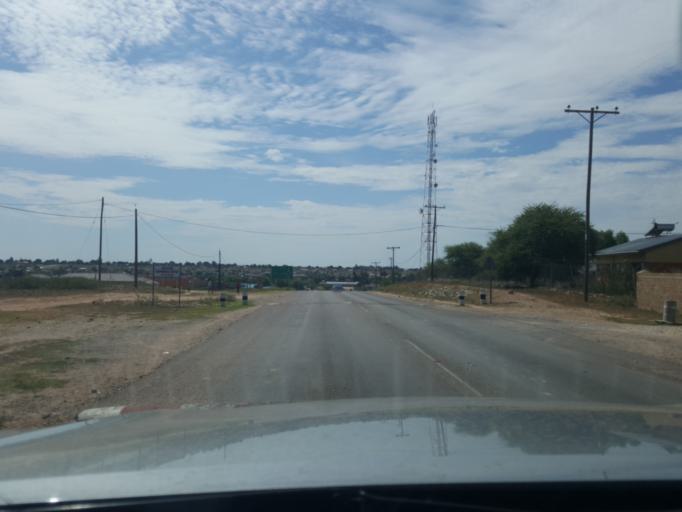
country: BW
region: Kweneng
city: Letlhakeng
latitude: -24.1038
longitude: 25.0314
